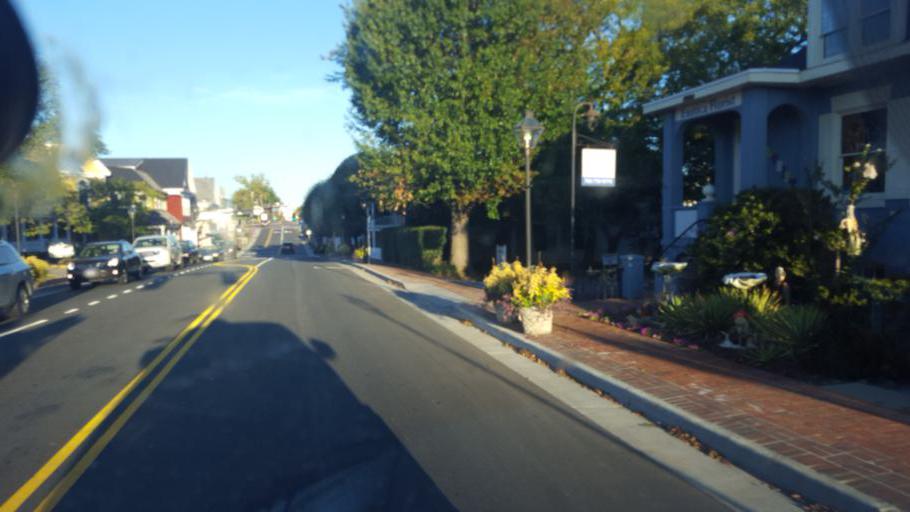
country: US
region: Virginia
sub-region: City of Fairfax
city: Fairfax
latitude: 38.8458
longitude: -77.3043
